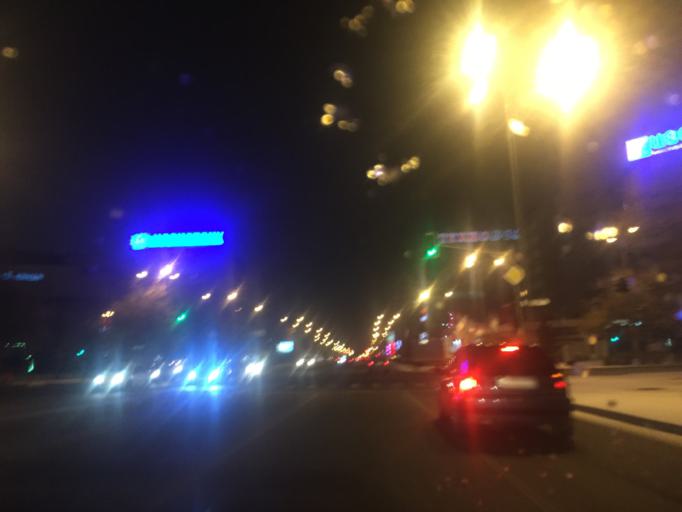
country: KZ
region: Astana Qalasy
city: Astana
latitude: 51.1710
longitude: 71.4259
